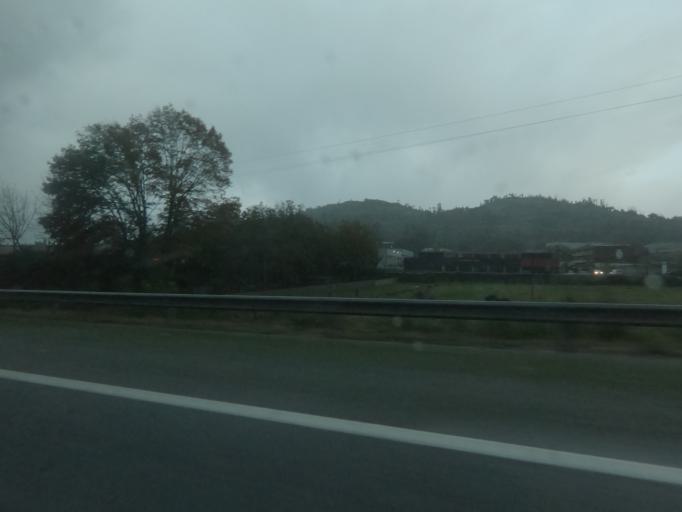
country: PT
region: Braga
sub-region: Braga
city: Braga
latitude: 41.5324
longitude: -8.4646
